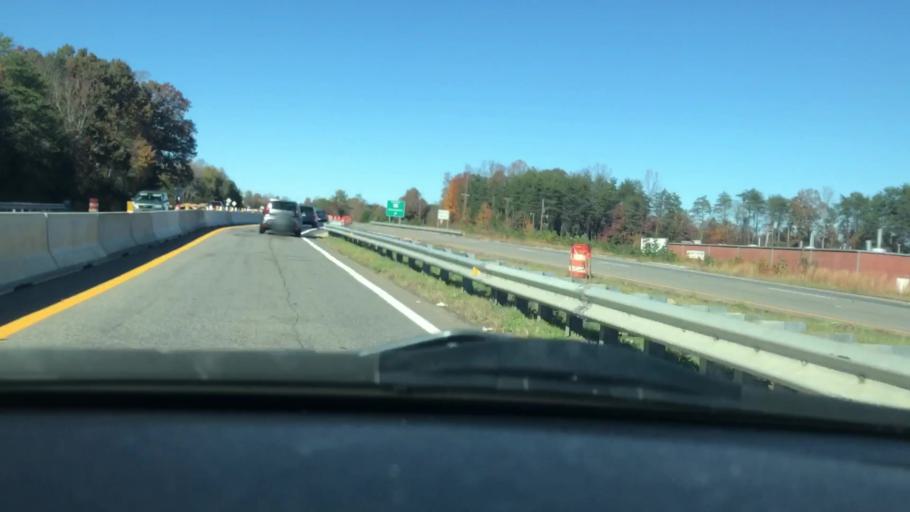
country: US
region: North Carolina
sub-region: Rockingham County
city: Stoneville
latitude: 36.4418
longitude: -79.9306
